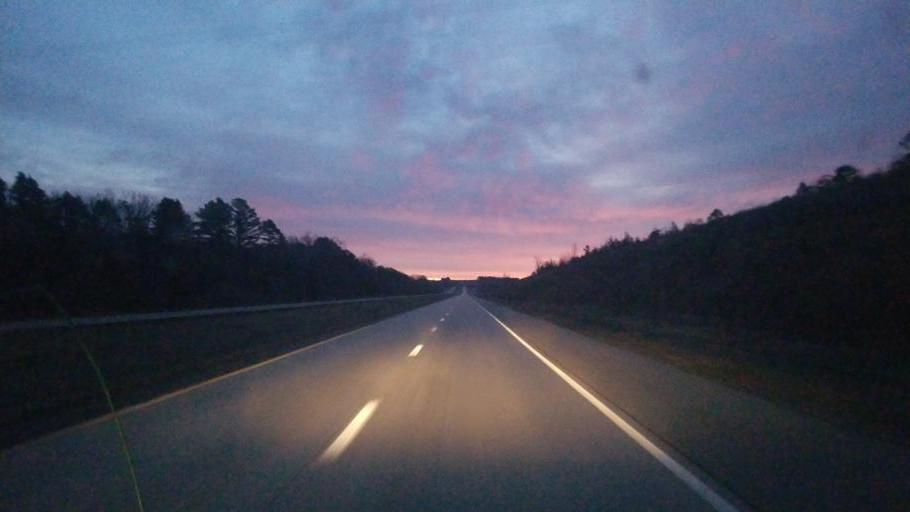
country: US
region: Missouri
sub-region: Shannon County
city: Winona
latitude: 36.9972
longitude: -91.4477
